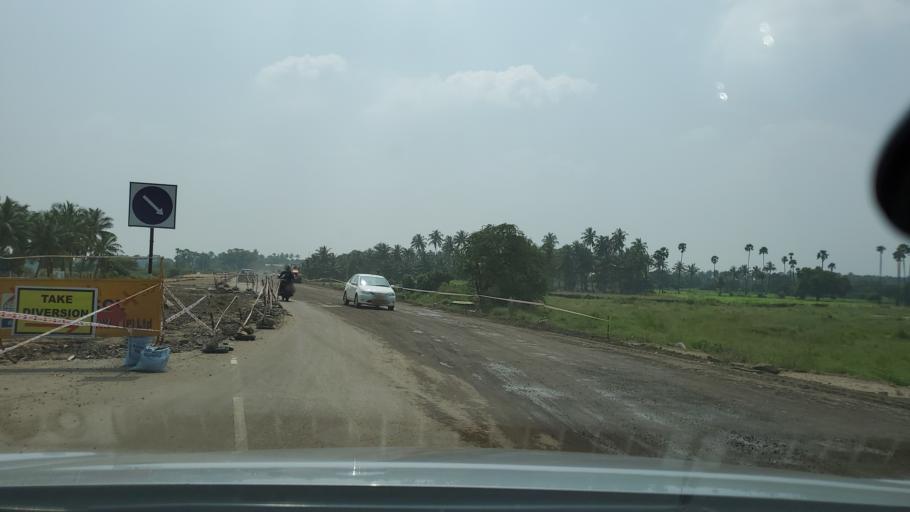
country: IN
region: Tamil Nadu
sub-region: Tiruppur
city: Kangayam
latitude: 10.9547
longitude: 77.4320
